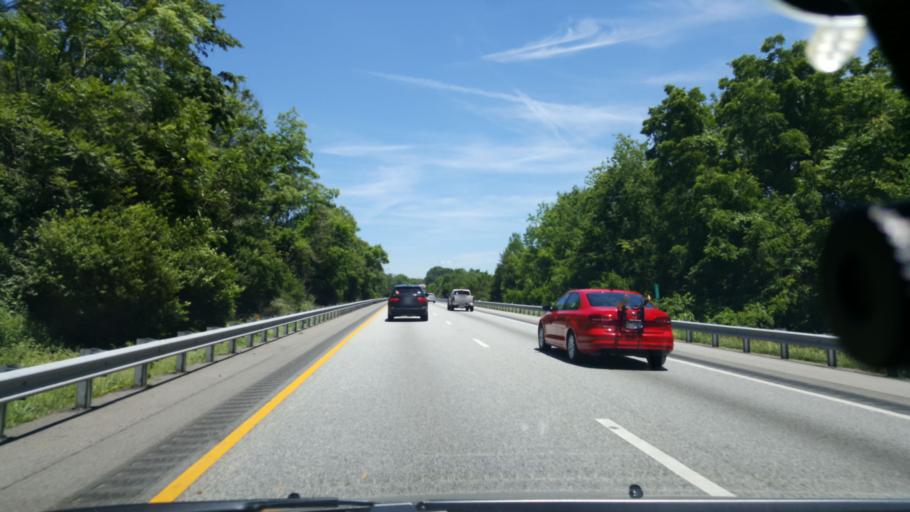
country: US
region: Virginia
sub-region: Botetourt County
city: Daleville
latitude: 37.4369
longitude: -79.8692
